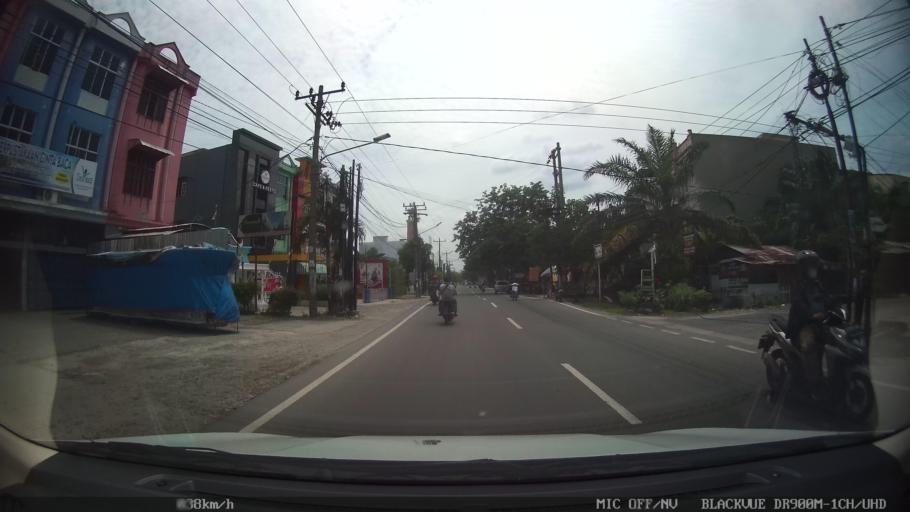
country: ID
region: North Sumatra
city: Sunggal
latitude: 3.5775
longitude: 98.6232
